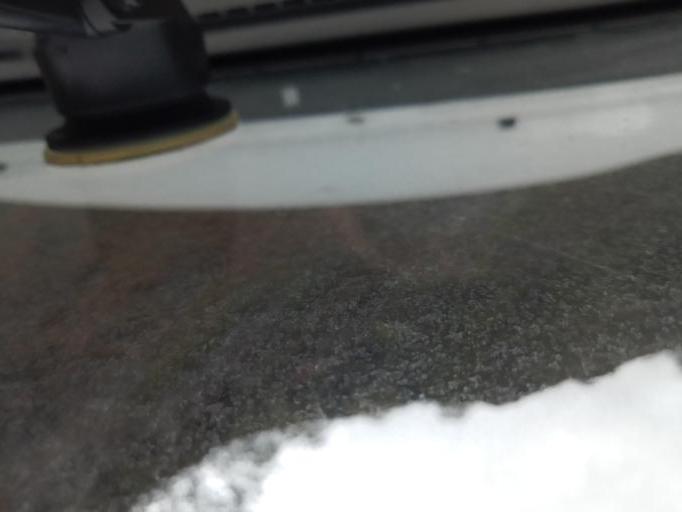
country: CV
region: Sao Salvador do Mundo
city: Picos
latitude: 15.1418
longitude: -23.6356
